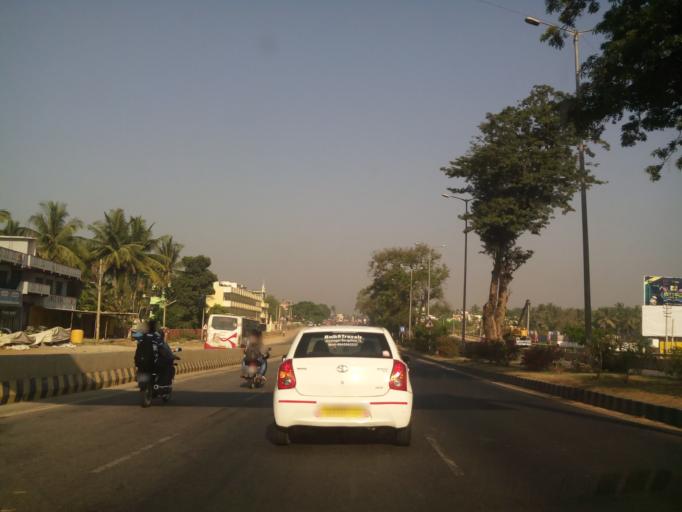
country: IN
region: Karnataka
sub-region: Bangalore Rural
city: Nelamangala
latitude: 13.0779
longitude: 77.4301
